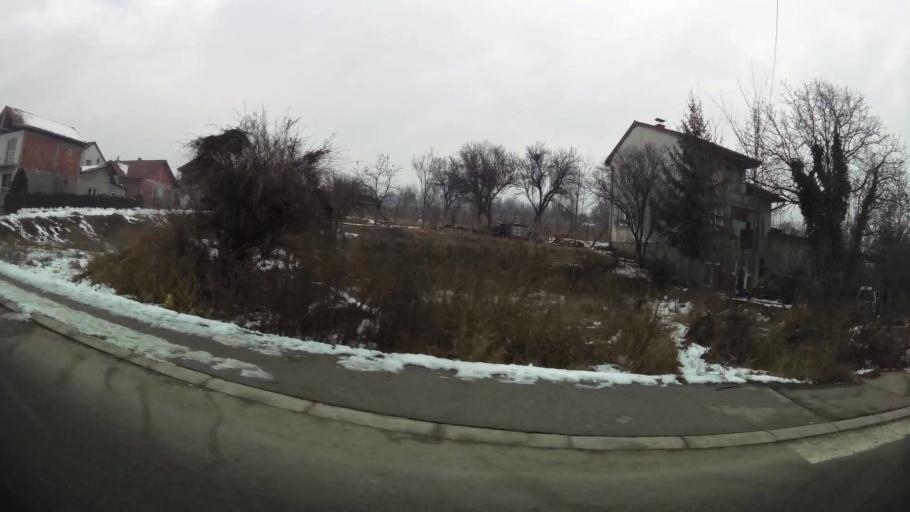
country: MK
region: Saraj
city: Saraj
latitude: 42.0307
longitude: 21.3462
